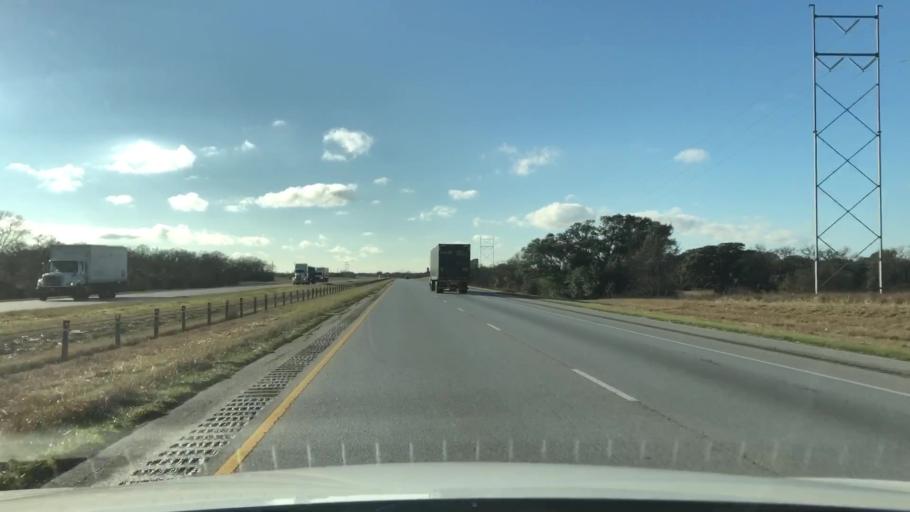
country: US
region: Texas
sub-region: Colorado County
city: Weimar
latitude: 29.6894
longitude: -96.6860
